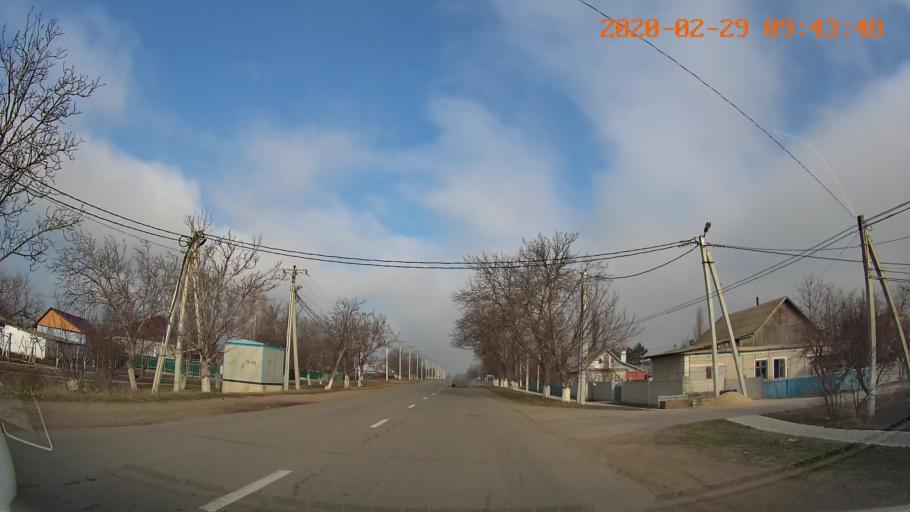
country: MD
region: Telenesti
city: Crasnoe
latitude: 46.6472
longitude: 29.8199
